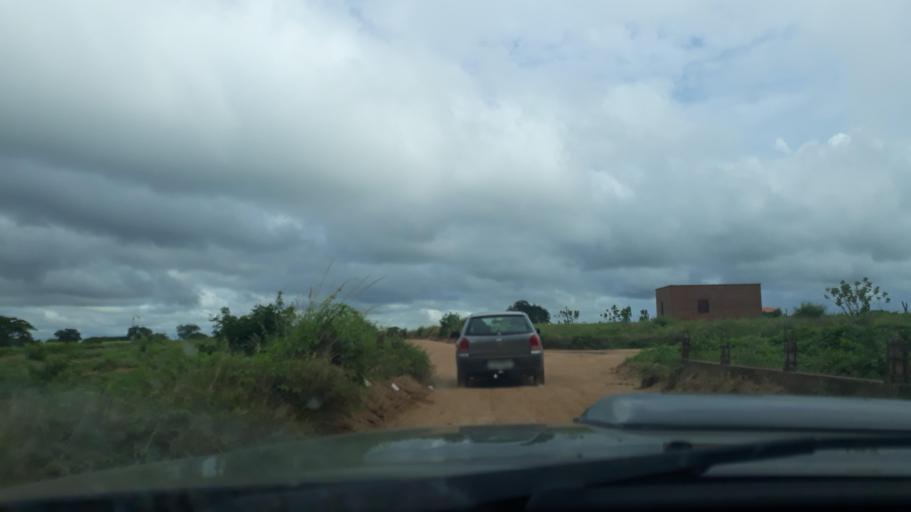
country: BR
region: Bahia
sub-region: Riacho De Santana
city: Riacho de Santana
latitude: -13.9088
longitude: -42.8523
